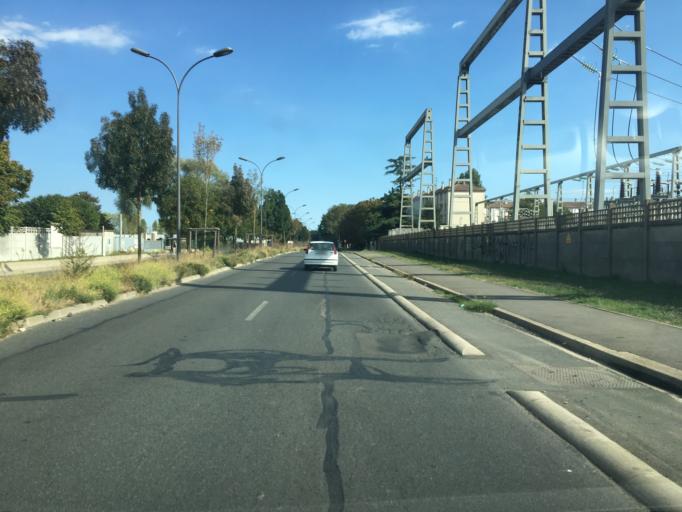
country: FR
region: Ile-de-France
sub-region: Departement du Val-de-Marne
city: Valenton
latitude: 48.7548
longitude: 2.4458
